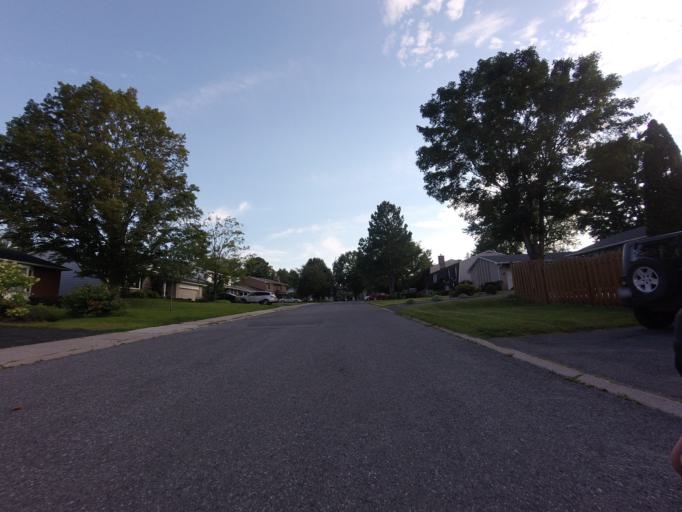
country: CA
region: Ontario
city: Bells Corners
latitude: 45.2803
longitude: -75.7691
